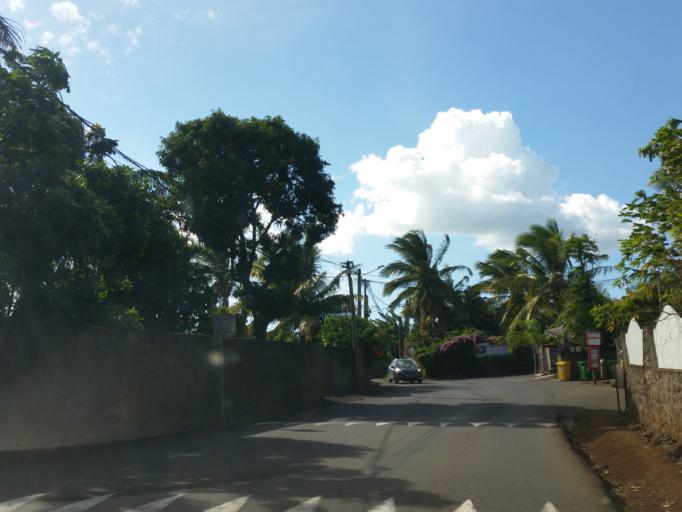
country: RE
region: Reunion
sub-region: Reunion
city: Saint-Pierre
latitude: -21.3291
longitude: 55.4903
